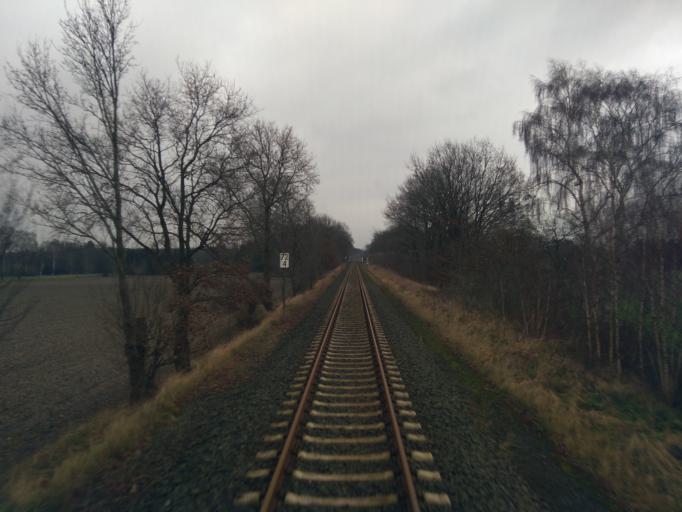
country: DE
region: Lower Saxony
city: Buchholz
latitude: 52.9712
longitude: 9.5372
